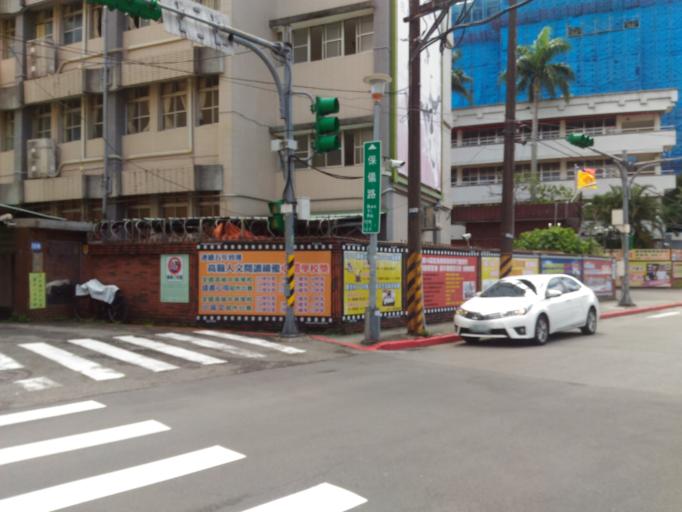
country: TW
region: Taipei
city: Taipei
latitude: 24.9858
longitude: 121.5675
